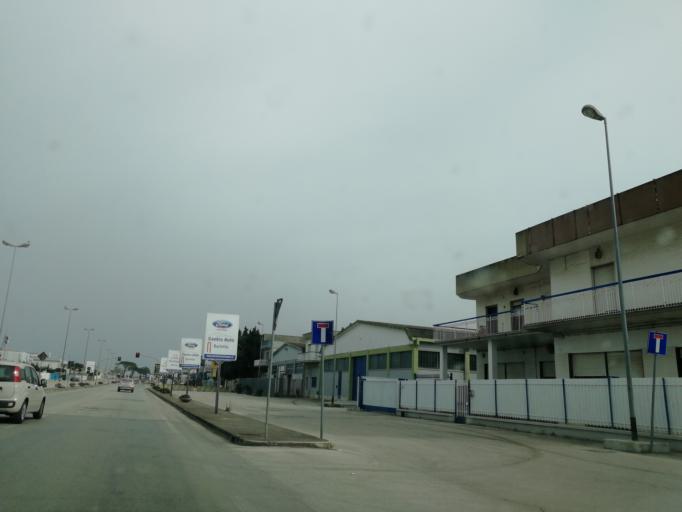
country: IT
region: Apulia
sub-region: Provincia di Barletta - Andria - Trani
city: Barletta
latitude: 41.3097
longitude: 16.3104
